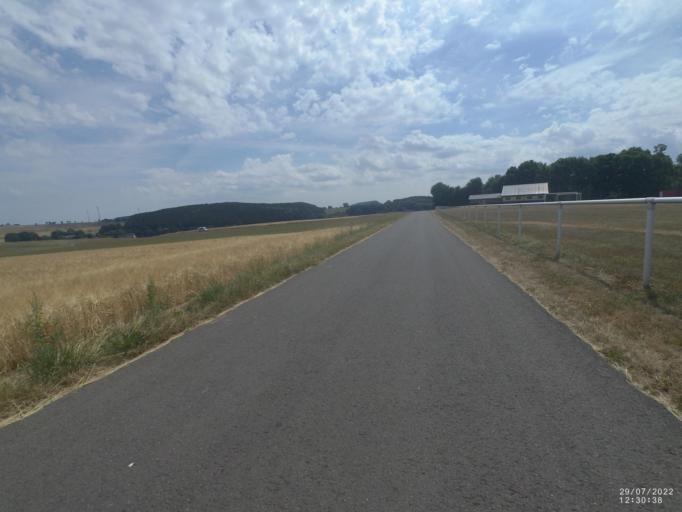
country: DE
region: Rheinland-Pfalz
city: Duppach
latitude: 50.2619
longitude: 6.5705
